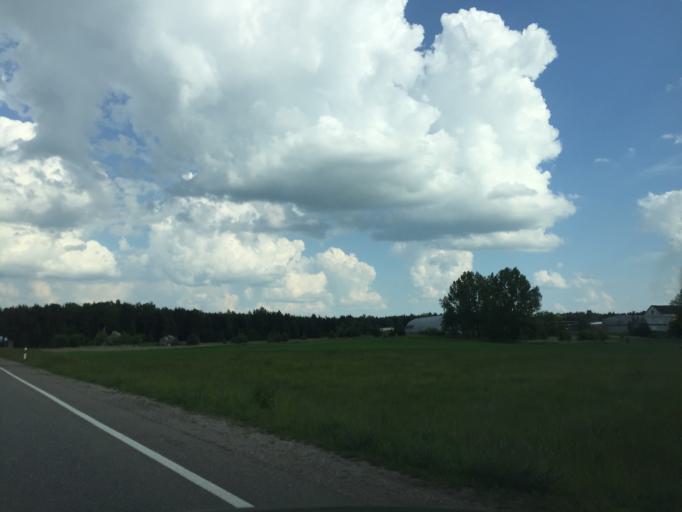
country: LT
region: Klaipedos apskritis
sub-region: Klaipeda
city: Palanga
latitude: 55.8982
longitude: 21.1515
